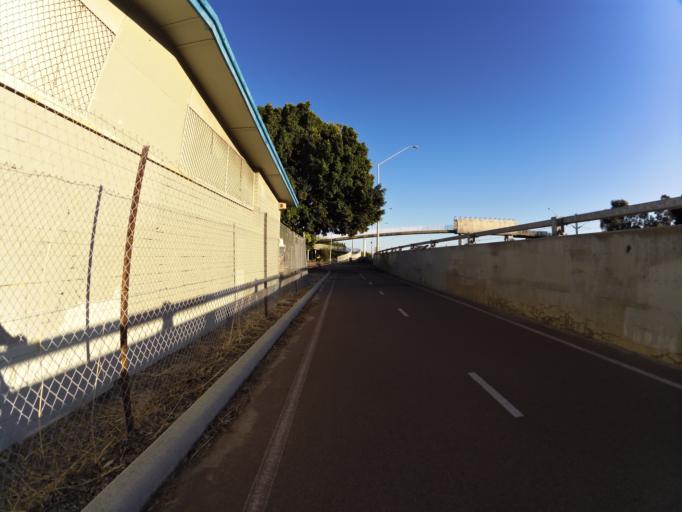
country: AU
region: Western Australia
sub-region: South Perth
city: Como
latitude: -32.0045
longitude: 115.8536
